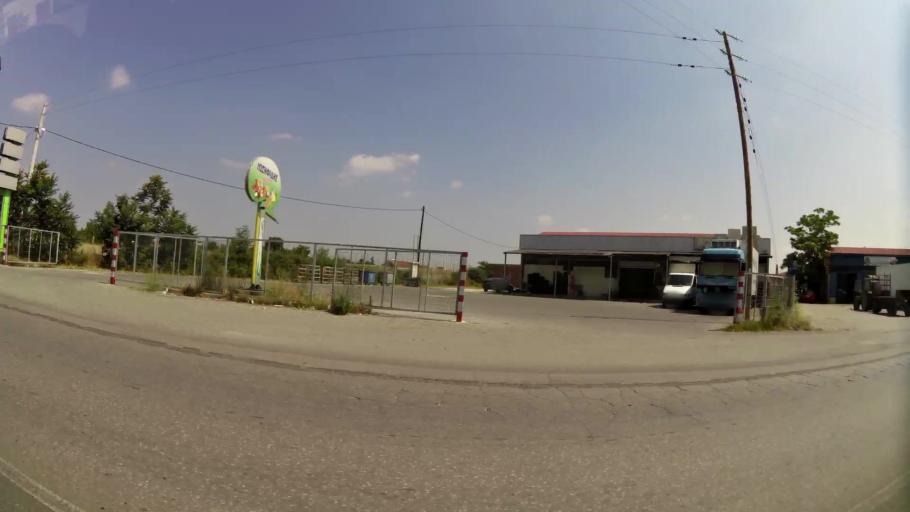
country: GR
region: Central Macedonia
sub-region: Nomos Imathias
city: Veroia
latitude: 40.5279
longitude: 22.2129
